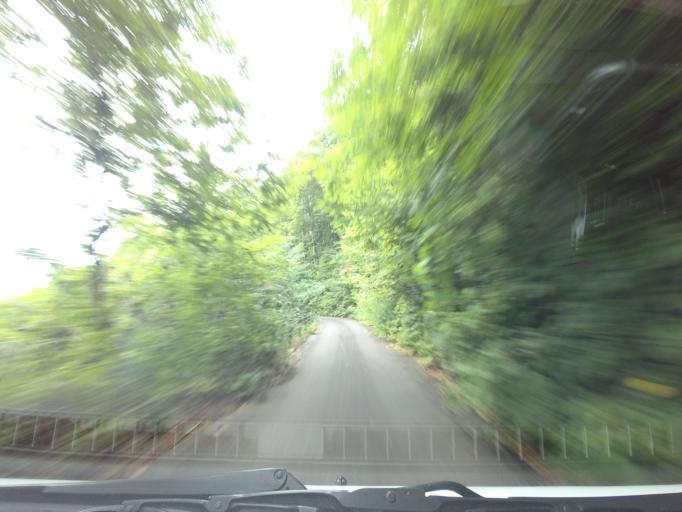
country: JP
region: Fukushima
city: Motomiya
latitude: 37.5591
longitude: 140.3026
